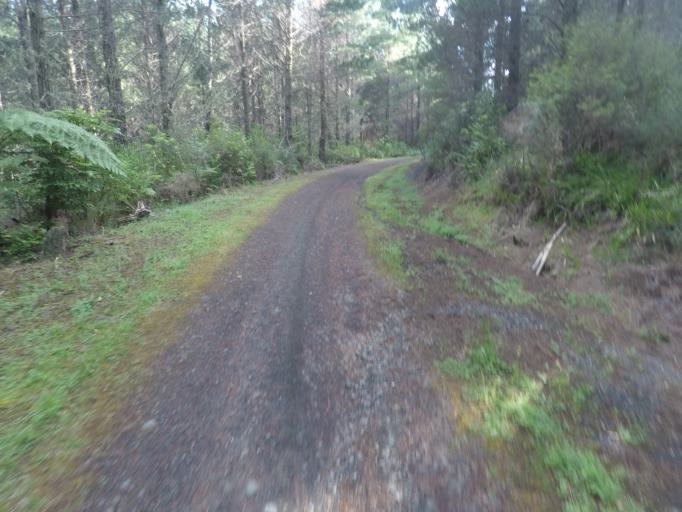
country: NZ
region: Auckland
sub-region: Auckland
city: Parakai
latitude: -36.7110
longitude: 174.5762
